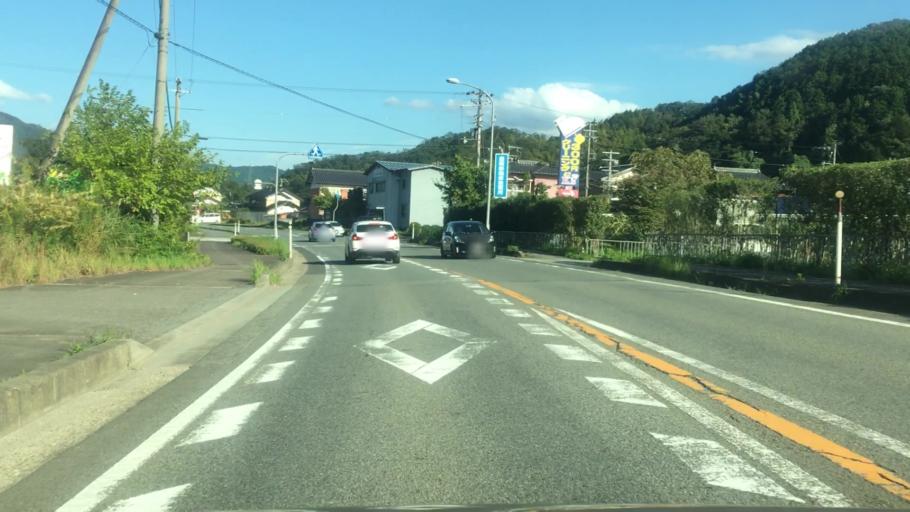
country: JP
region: Hyogo
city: Toyooka
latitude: 35.5548
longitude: 134.8351
